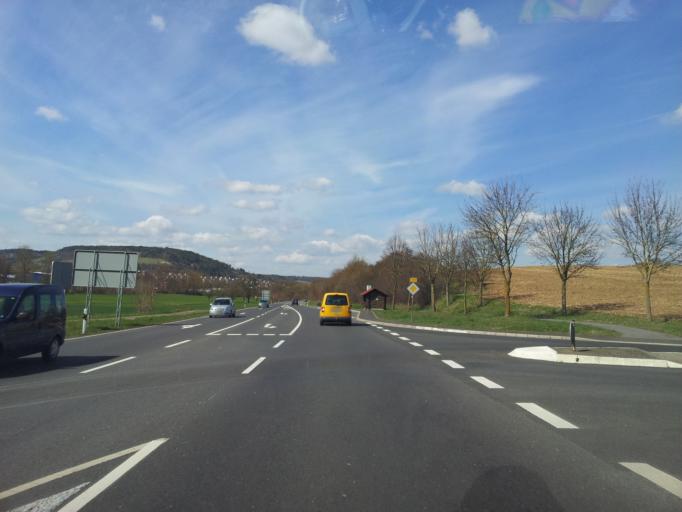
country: DE
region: Baden-Wuerttemberg
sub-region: Regierungsbezirk Stuttgart
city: Lauda-Konigshofen
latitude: 49.5624
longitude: 9.7203
